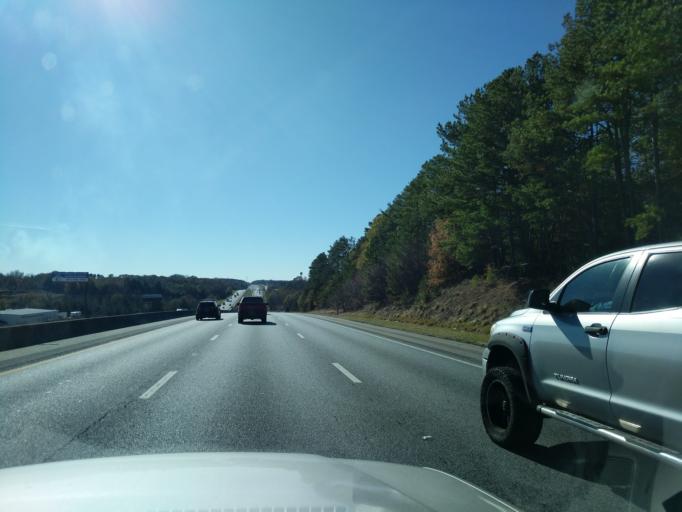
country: US
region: South Carolina
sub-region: Greenville County
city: Golden Grove
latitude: 34.7397
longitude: -82.4852
